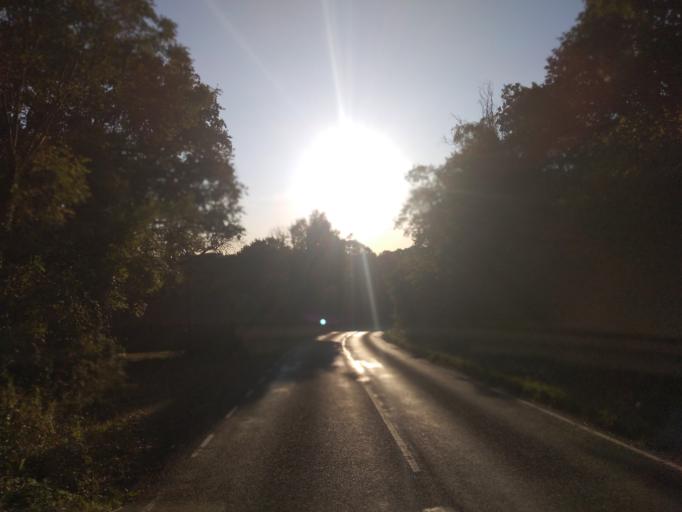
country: GB
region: England
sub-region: West Sussex
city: Goring-by-Sea
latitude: 50.8371
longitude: -0.4425
